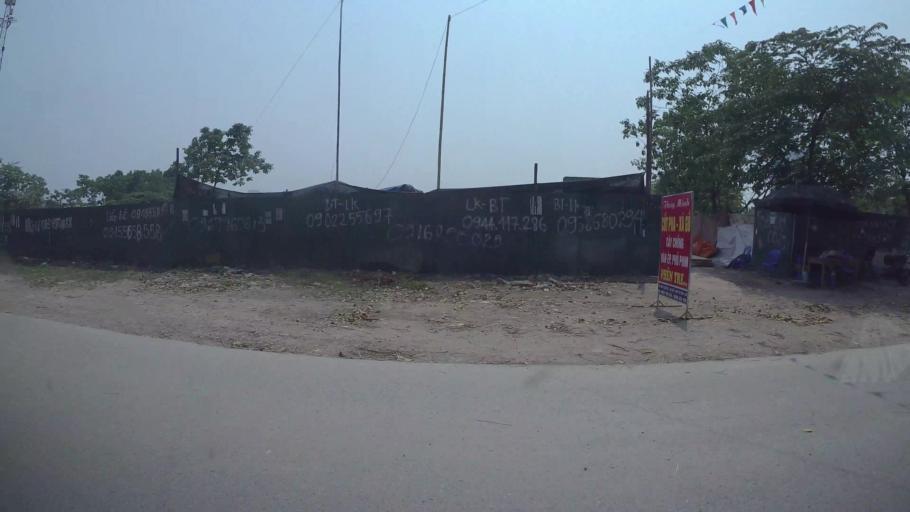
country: VN
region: Ha Noi
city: Ha Dong
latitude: 20.9918
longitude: 105.7626
